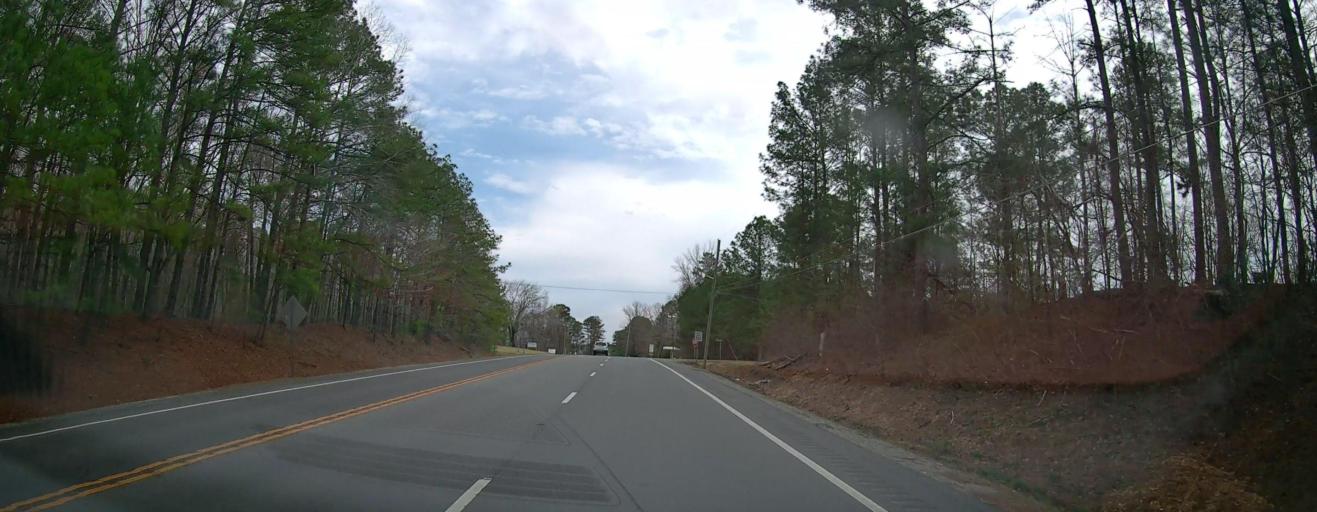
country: US
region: Alabama
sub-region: Marion County
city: Guin
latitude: 33.9880
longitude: -87.9231
